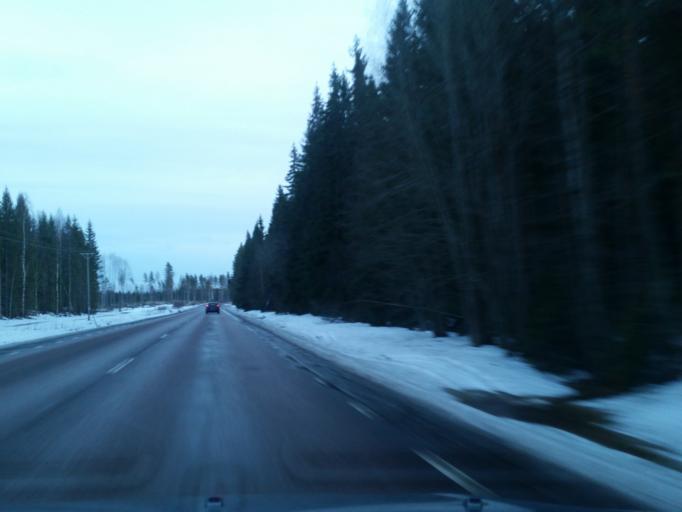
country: SE
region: Gaevleborg
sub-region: Sandvikens Kommun
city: Sandviken
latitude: 60.6501
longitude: 16.7290
